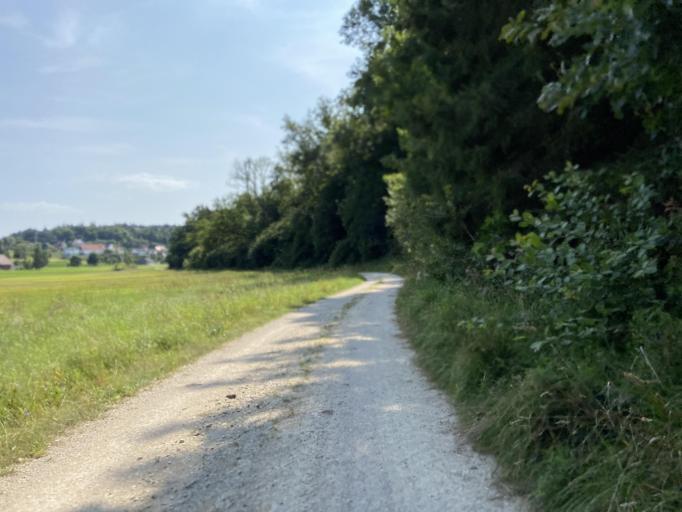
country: DE
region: Baden-Wuerttemberg
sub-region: Tuebingen Region
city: Bingen
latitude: 48.1130
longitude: 9.2920
